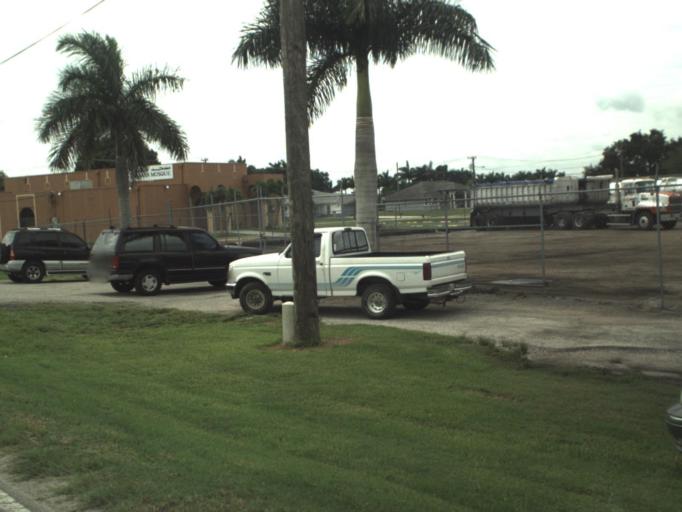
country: US
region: Florida
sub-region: Palm Beach County
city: Belle Glade
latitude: 26.6821
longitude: -80.6598
